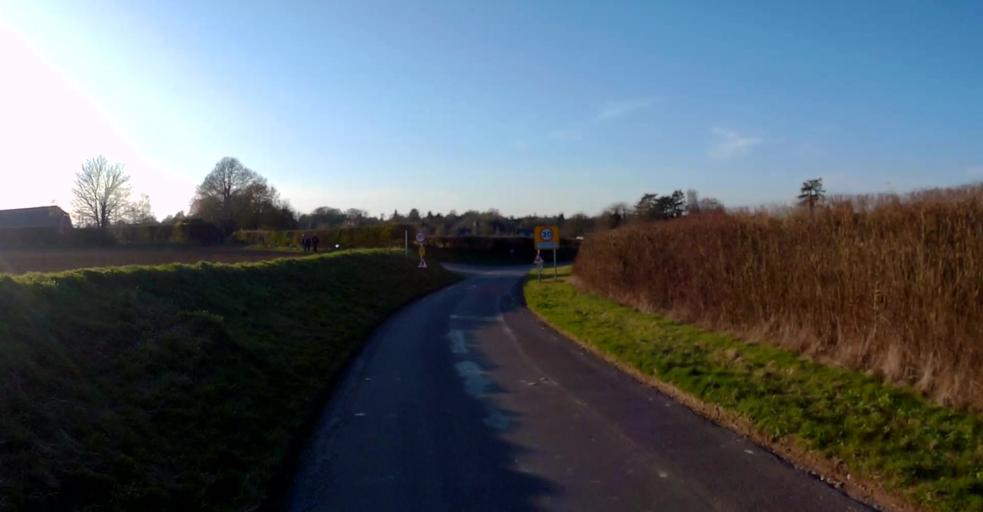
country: GB
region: England
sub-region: Hampshire
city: Basingstoke
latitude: 51.2355
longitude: -1.0936
